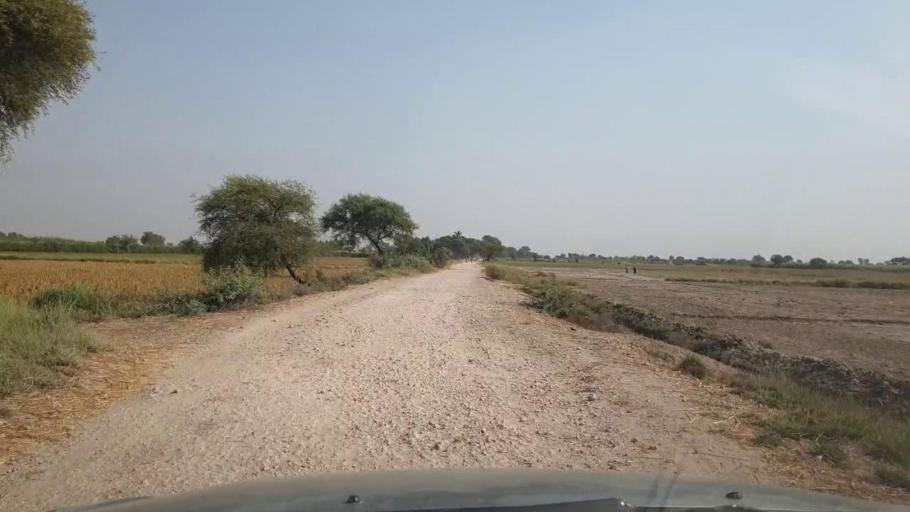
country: PK
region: Sindh
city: Bulri
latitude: 24.9109
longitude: 68.3687
